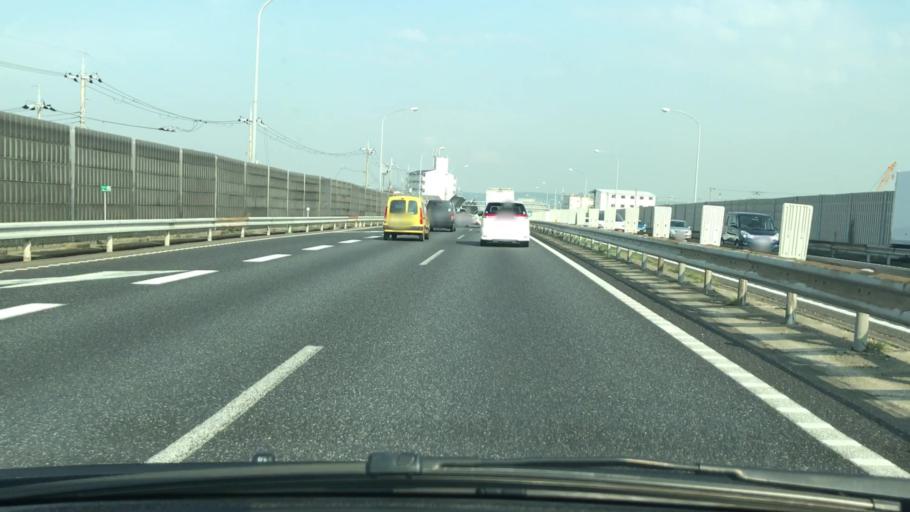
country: JP
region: Hyogo
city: Akashi
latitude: 34.6808
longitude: 135.0014
